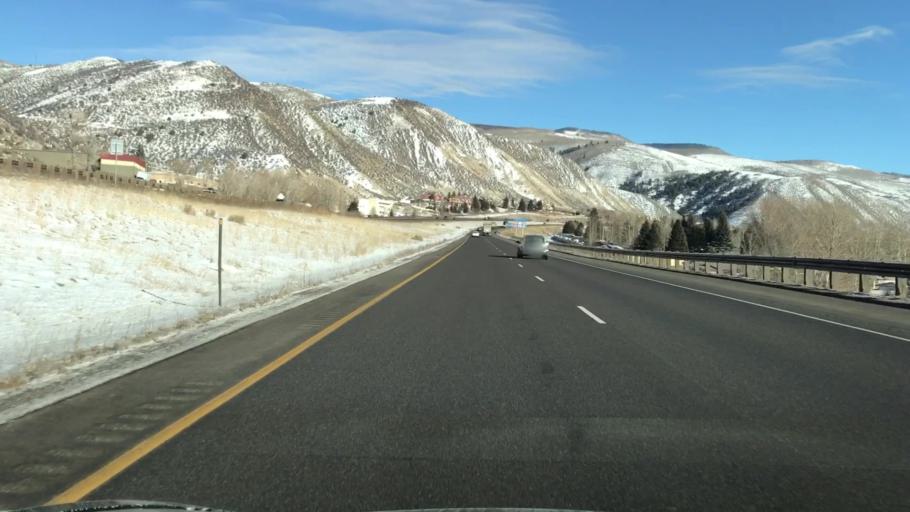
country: US
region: Colorado
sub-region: Eagle County
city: Avon
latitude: 39.6382
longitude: -106.5420
